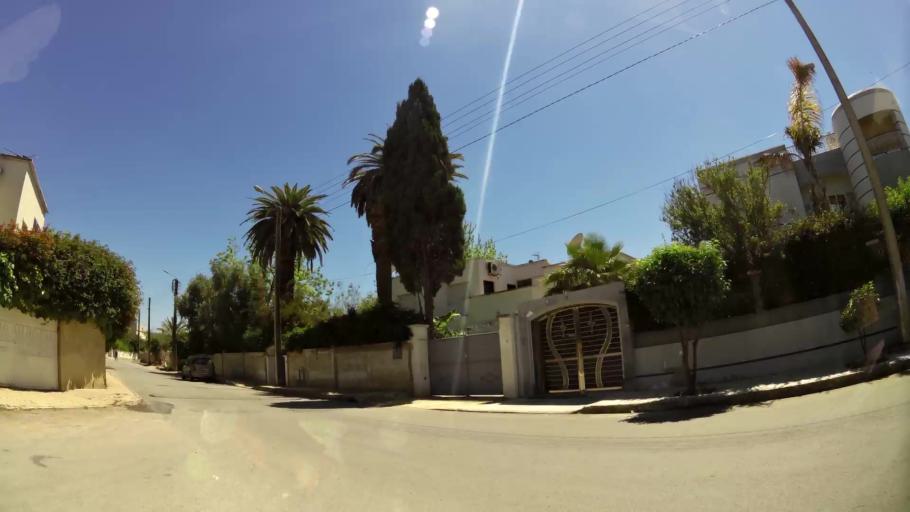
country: MA
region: Fes-Boulemane
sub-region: Fes
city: Fes
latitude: 34.0235
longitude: -5.0014
